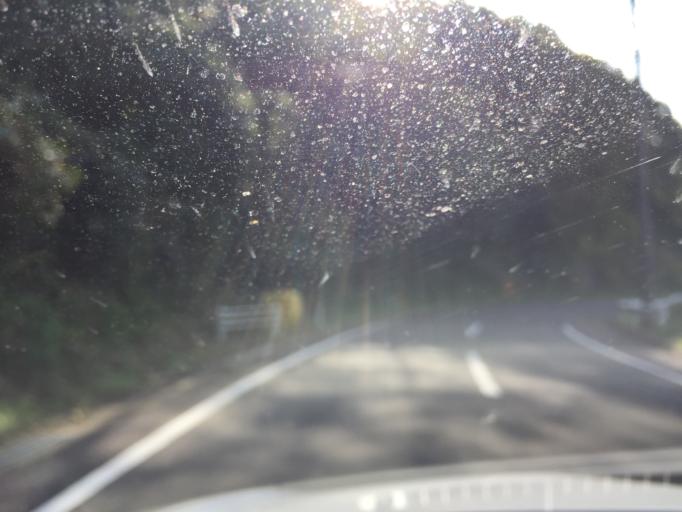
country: JP
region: Fukushima
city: Ishikawa
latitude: 37.1728
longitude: 140.4704
